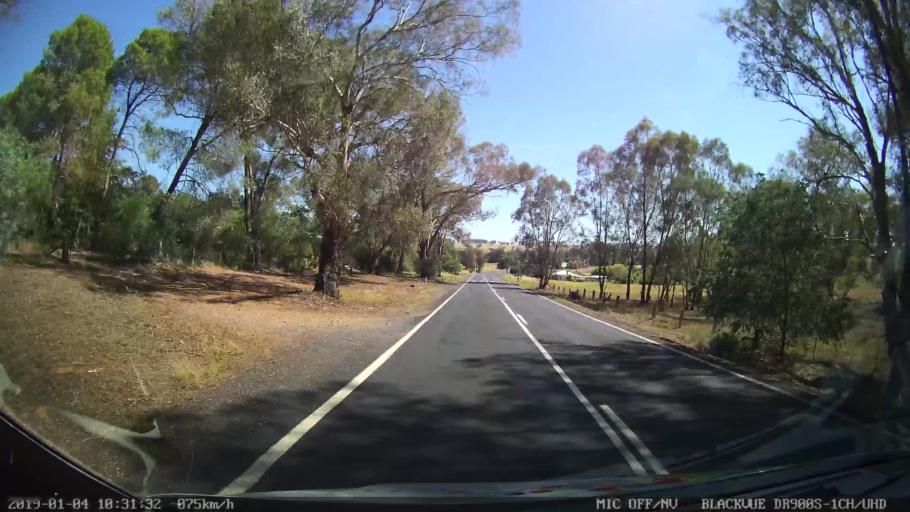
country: AU
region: New South Wales
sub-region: Cabonne
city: Canowindra
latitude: -33.3337
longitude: 148.6325
